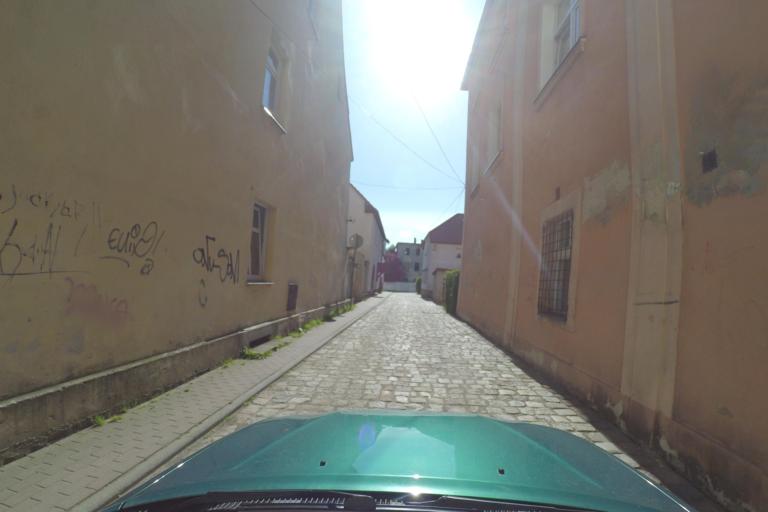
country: PL
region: Lower Silesian Voivodeship
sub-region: Powiat kamiennogorski
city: Lubawka
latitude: 50.7065
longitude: 16.0001
